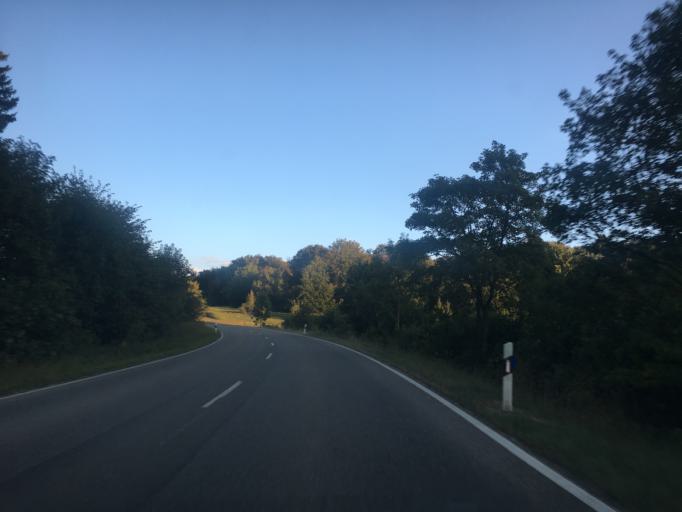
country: DE
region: Baden-Wuerttemberg
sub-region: Tuebingen Region
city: Pfullingen
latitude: 48.3992
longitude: 9.2637
